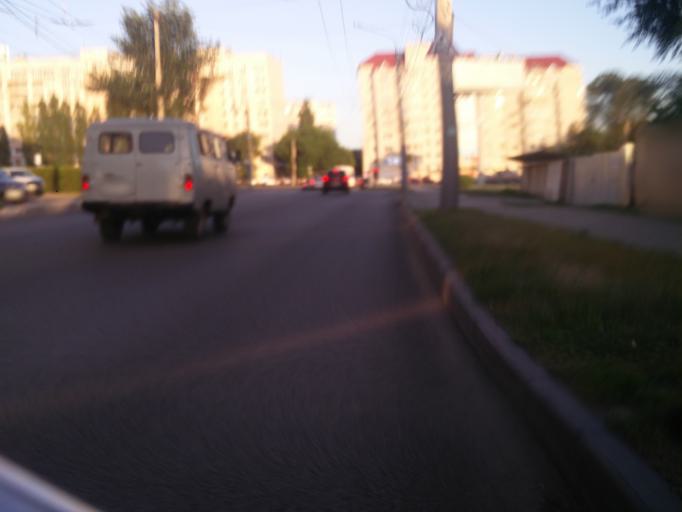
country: RU
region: Voronezj
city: Voronezh
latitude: 51.6485
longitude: 39.1549
